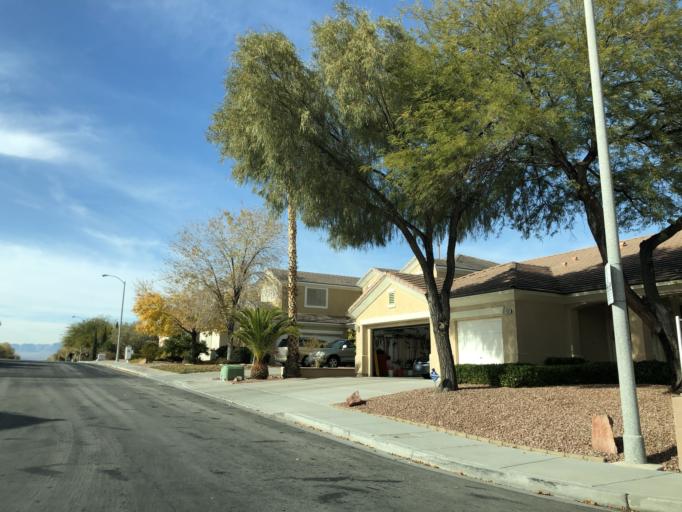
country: US
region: Nevada
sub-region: Clark County
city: Whitney
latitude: 36.0091
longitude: -115.0915
